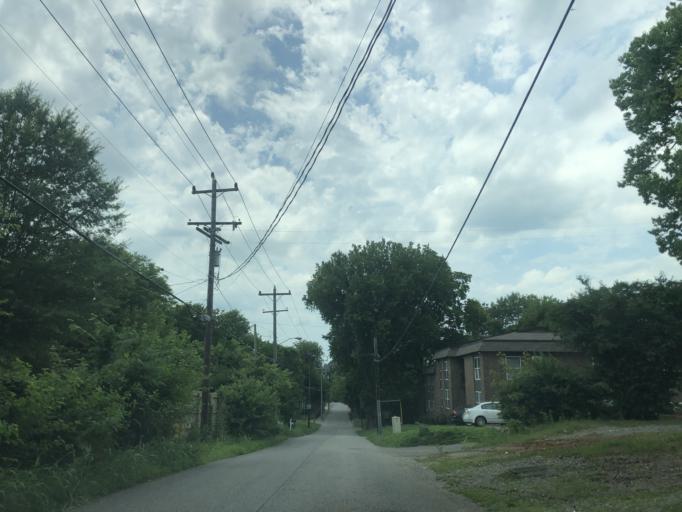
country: US
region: Tennessee
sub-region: Davidson County
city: Nashville
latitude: 36.1851
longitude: -86.7448
